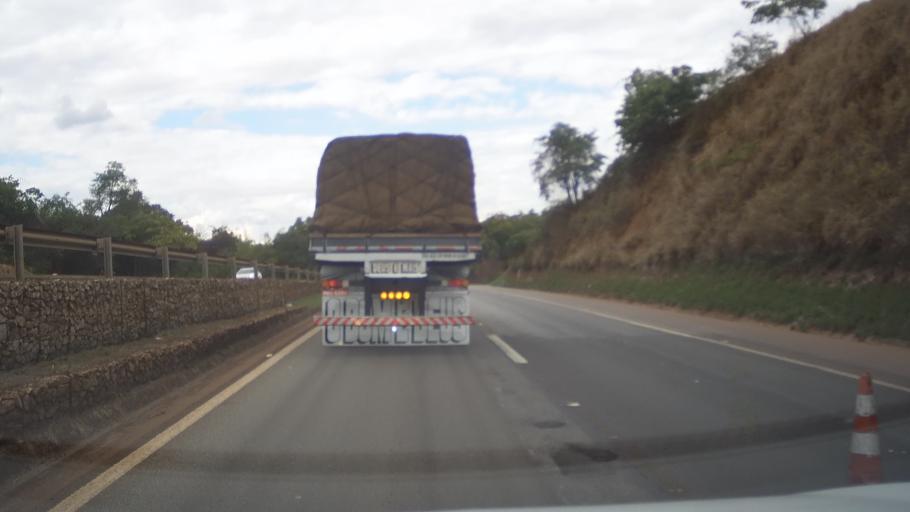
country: BR
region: Minas Gerais
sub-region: Itauna
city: Itauna
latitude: -20.3165
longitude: -44.4535
